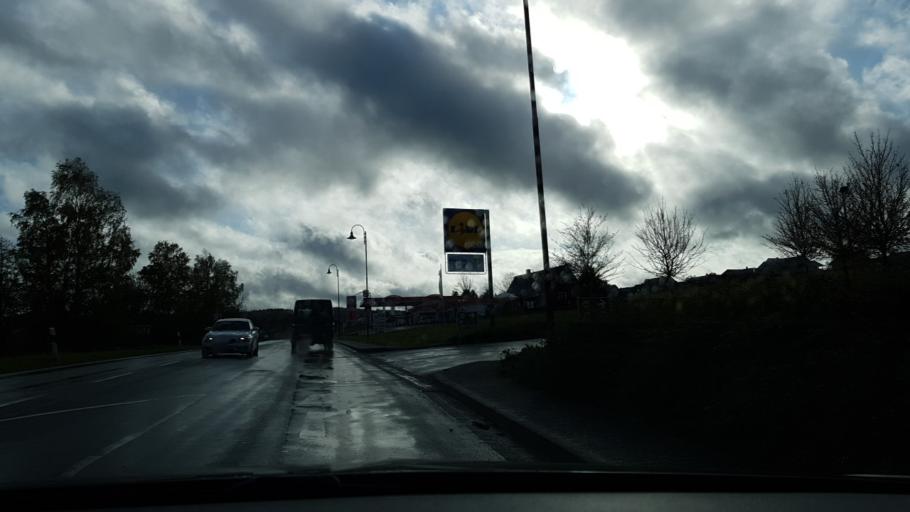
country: DE
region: Rheinland-Pfalz
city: Kelberg
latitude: 50.2947
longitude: 6.9213
